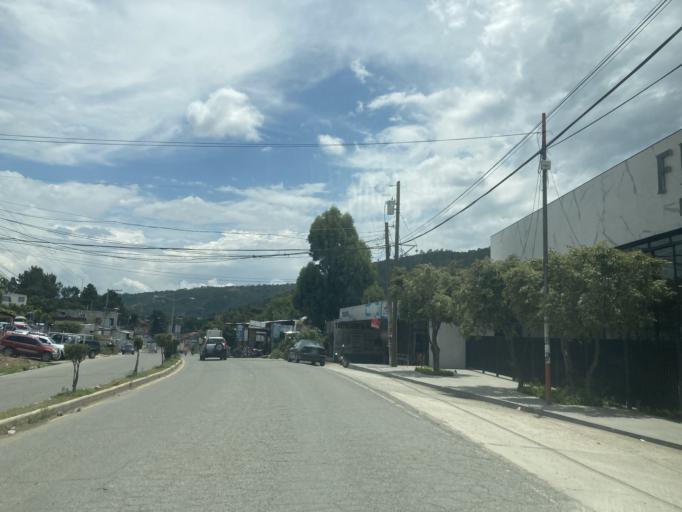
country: GT
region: Huehuetenango
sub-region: Municipio de Huehuetenango
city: Huehuetenango
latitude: 15.2997
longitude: -91.4929
